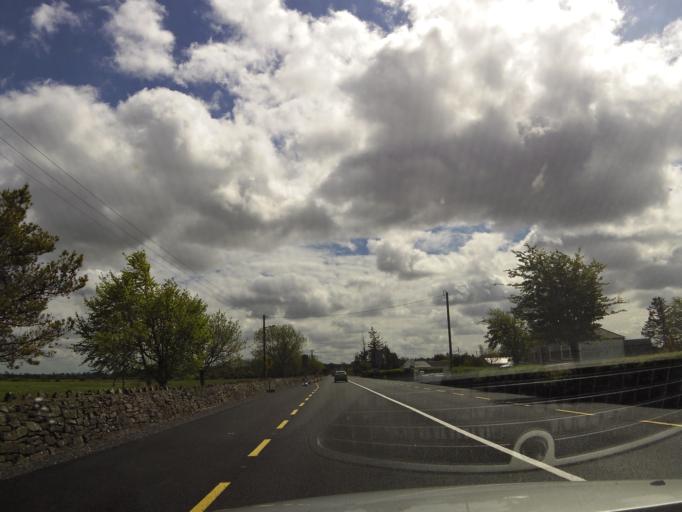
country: IE
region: Connaught
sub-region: County Galway
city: Tuam
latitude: 53.6097
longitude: -8.8949
